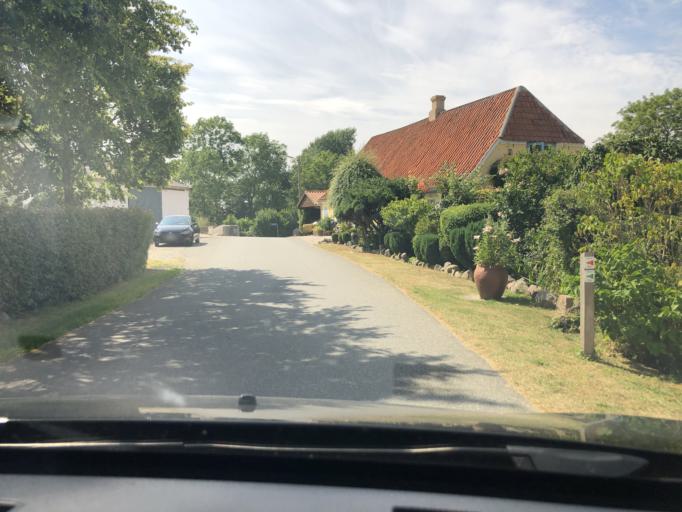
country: DK
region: South Denmark
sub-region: AEro Kommune
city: AEroskobing
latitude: 54.9139
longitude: 10.2994
